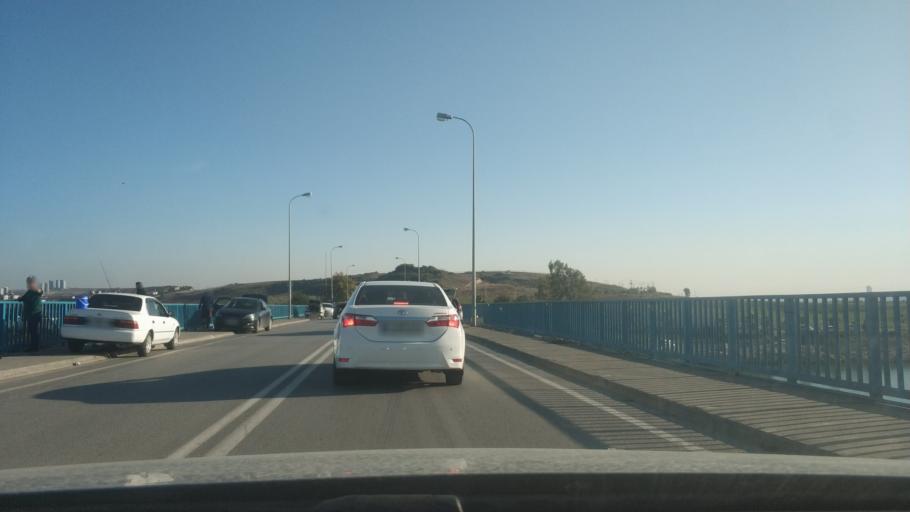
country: TR
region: Adana
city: Adana
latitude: 37.0994
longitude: 35.3036
